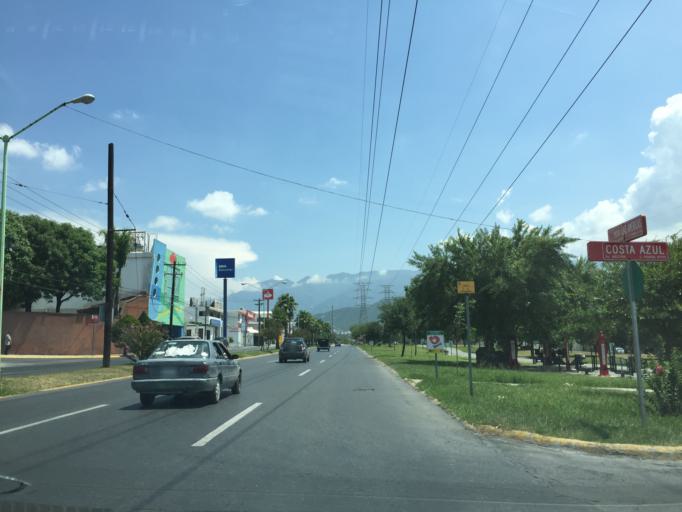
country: MX
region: Nuevo Leon
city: Guadalupe
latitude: 25.6450
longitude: -100.2683
